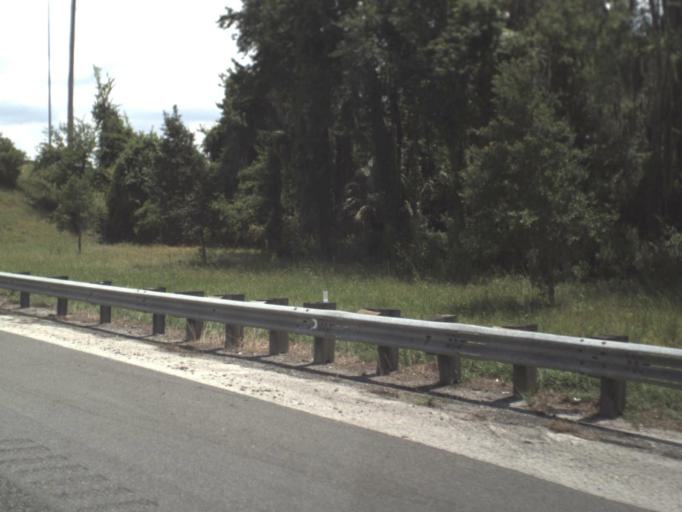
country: US
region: Florida
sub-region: Hamilton County
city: Jasper
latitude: 30.4489
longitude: -82.9337
